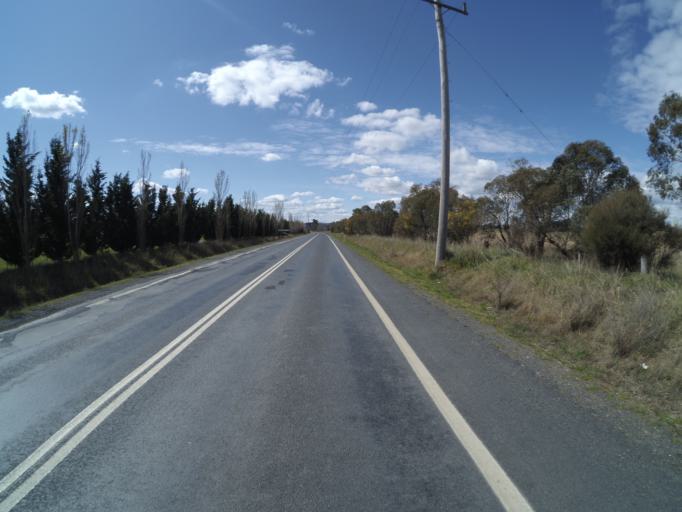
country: AU
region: New South Wales
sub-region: Goulburn Mulwaree
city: Goulburn
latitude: -34.7925
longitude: 149.6969
